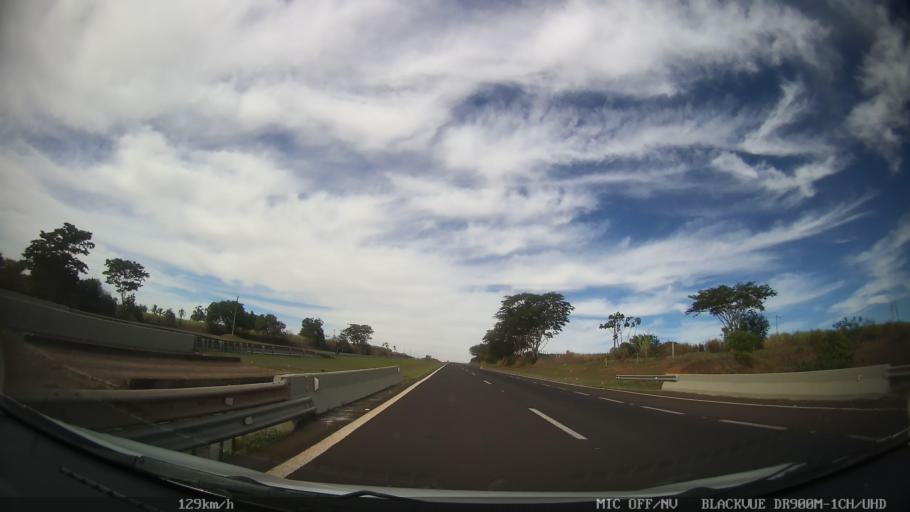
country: BR
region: Sao Paulo
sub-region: Taquaritinga
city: Taquaritinga
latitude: -21.5412
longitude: -48.5036
